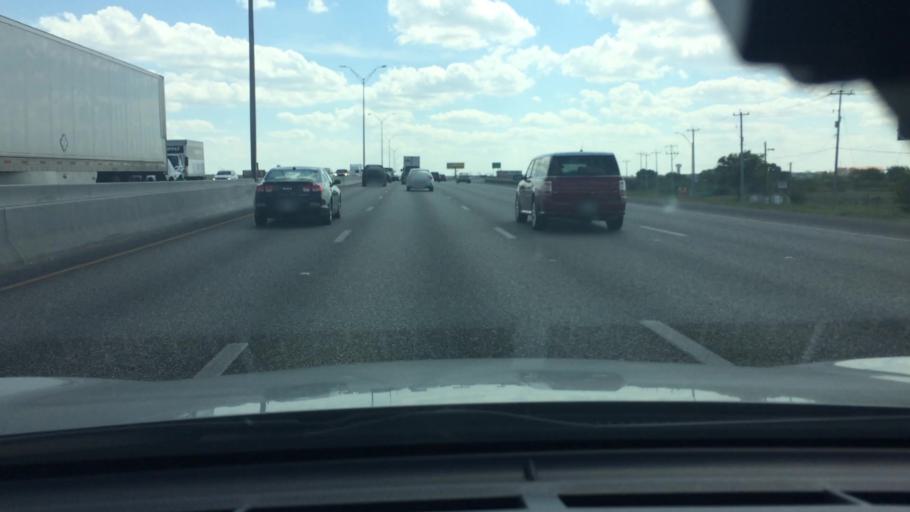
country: US
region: Texas
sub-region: Bexar County
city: Selma
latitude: 29.5876
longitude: -98.3017
